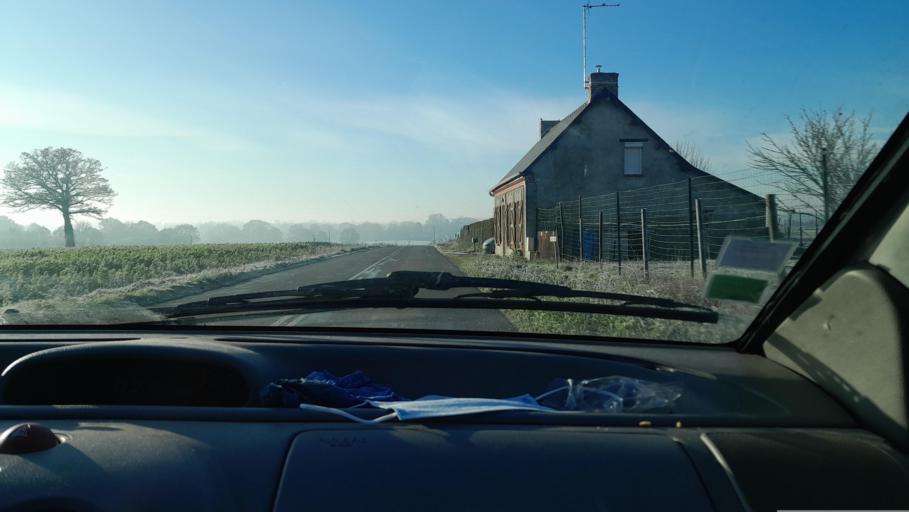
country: FR
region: Pays de la Loire
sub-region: Departement de la Mayenne
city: Ballots
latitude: 47.9093
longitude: -1.1015
